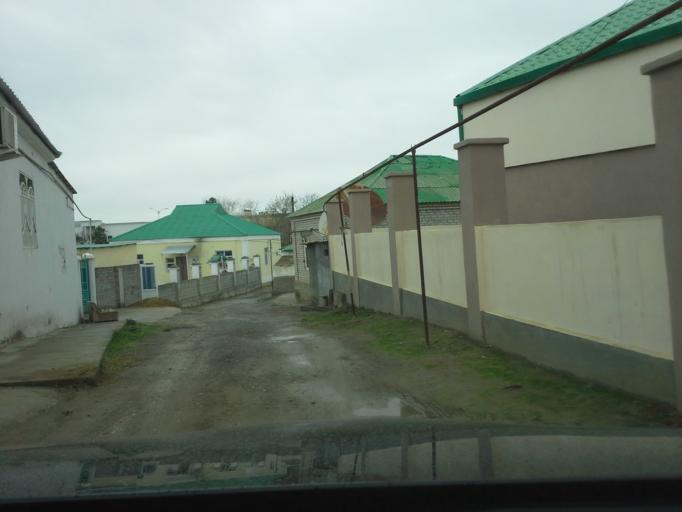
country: TM
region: Ahal
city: Abadan
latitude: 37.9603
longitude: 58.2248
